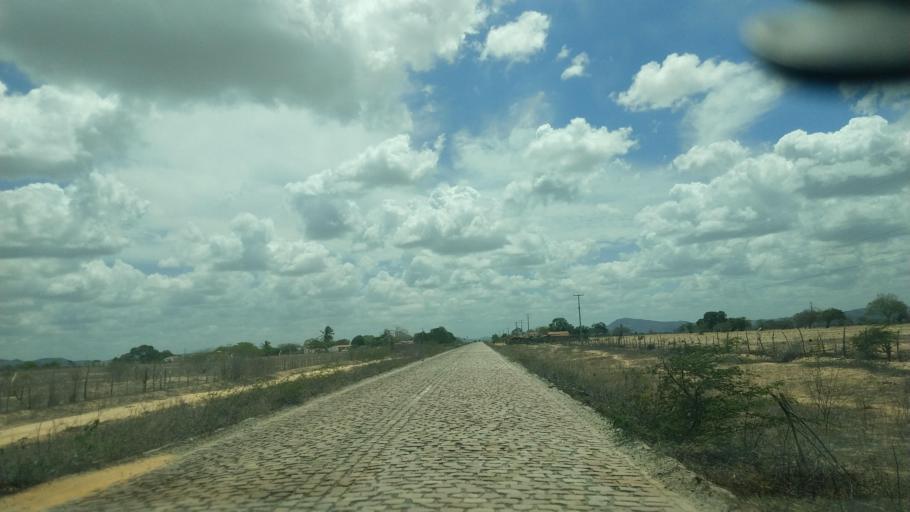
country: BR
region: Rio Grande do Norte
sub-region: Sao Paulo Do Potengi
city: Sao Paulo do Potengi
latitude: -5.9776
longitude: -35.8564
